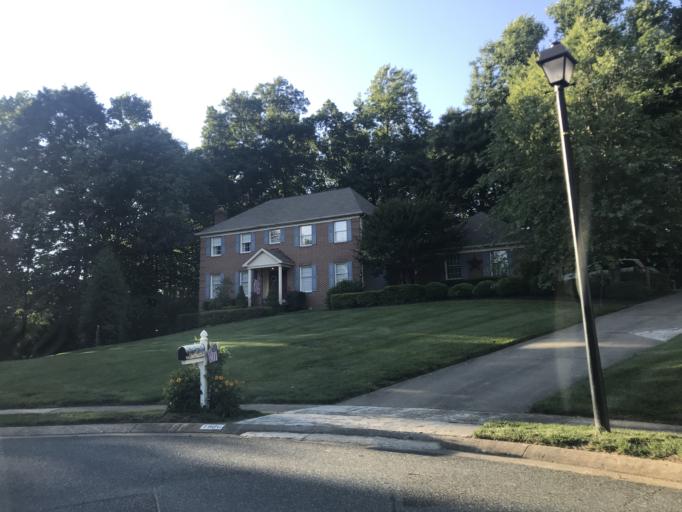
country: US
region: Maryland
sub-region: Harford County
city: South Bel Air
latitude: 39.5607
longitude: -76.3177
